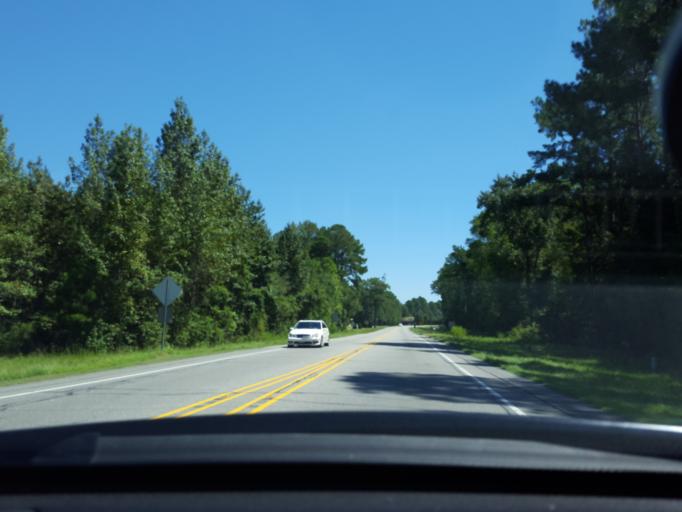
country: US
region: North Carolina
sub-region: Bladen County
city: Elizabethtown
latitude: 34.6454
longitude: -78.5901
